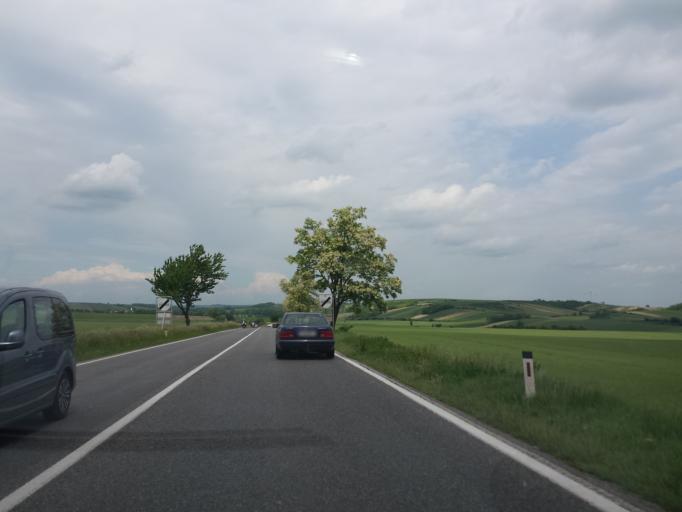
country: AT
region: Lower Austria
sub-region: Politischer Bezirk Mistelbach
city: Wilfersdorf
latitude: 48.5993
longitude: 16.6468
